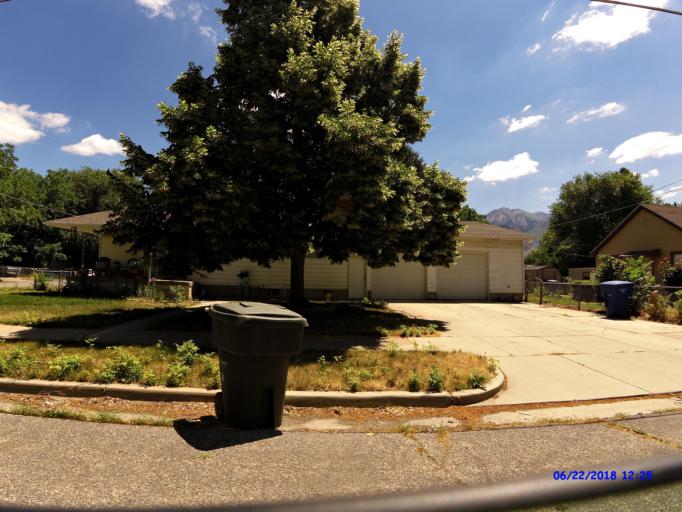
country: US
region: Utah
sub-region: Weber County
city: Ogden
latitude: 41.2394
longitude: -111.9644
